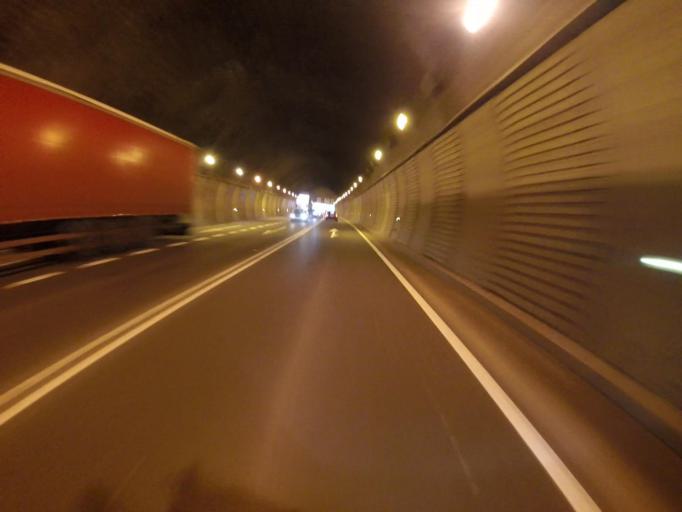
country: ES
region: Basque Country
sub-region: Provincia de Guipuzcoa
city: Lezo
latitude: 43.3170
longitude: -1.8988
